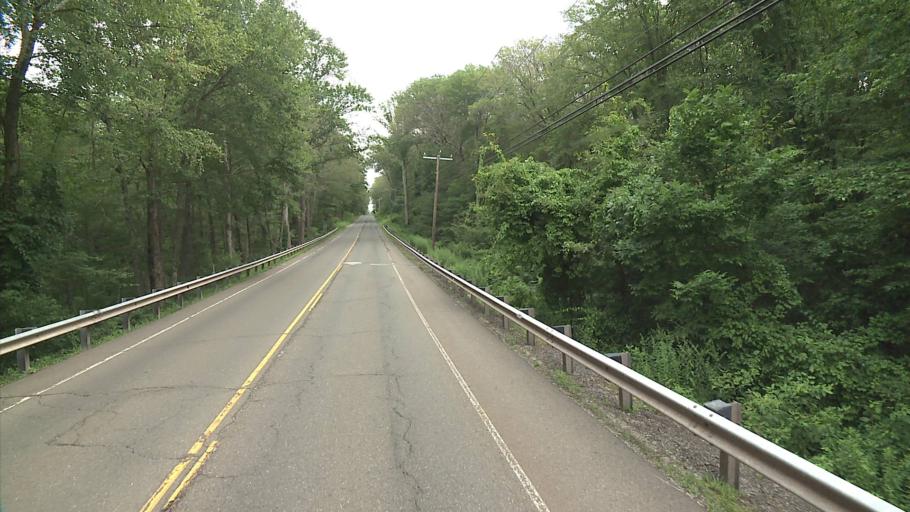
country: US
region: Connecticut
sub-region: Middlesex County
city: Clinton
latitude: 41.3567
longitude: -72.5367
